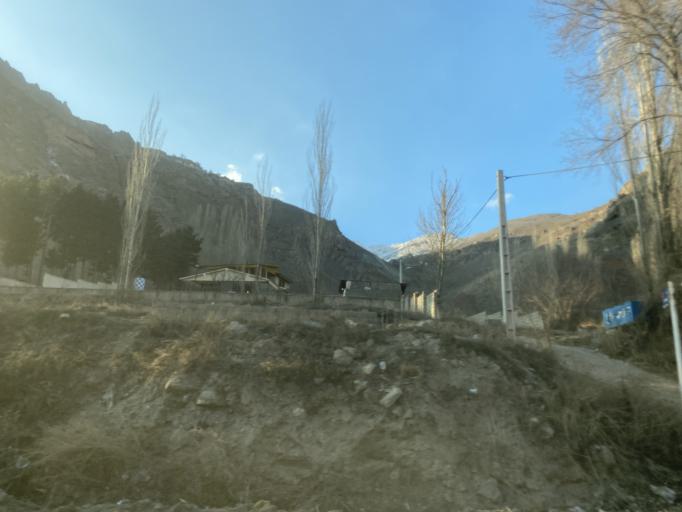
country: IR
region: Tehran
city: Damavand
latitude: 35.8927
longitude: 52.2073
